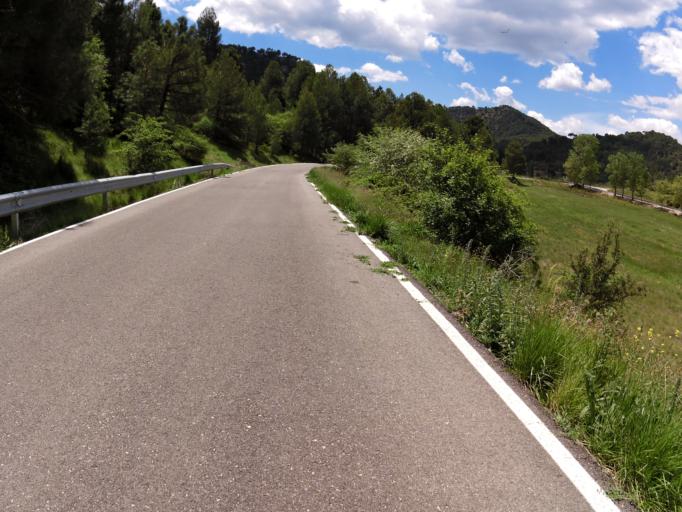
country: ES
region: Castille-La Mancha
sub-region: Provincia de Albacete
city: Paterna del Madera
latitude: 38.5694
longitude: -2.3845
